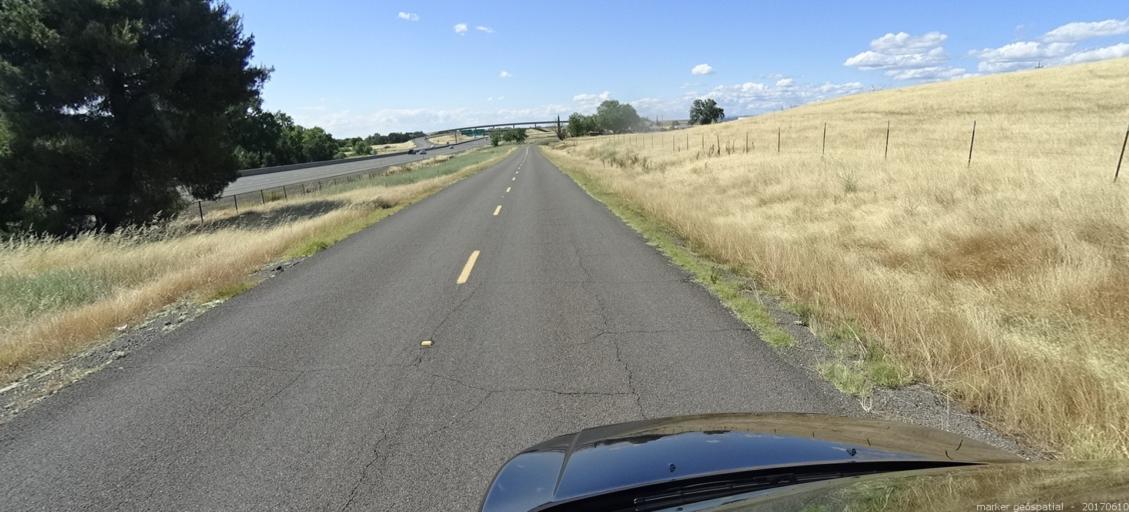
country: US
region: California
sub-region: Butte County
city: Thermalito
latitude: 39.5758
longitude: -121.6165
